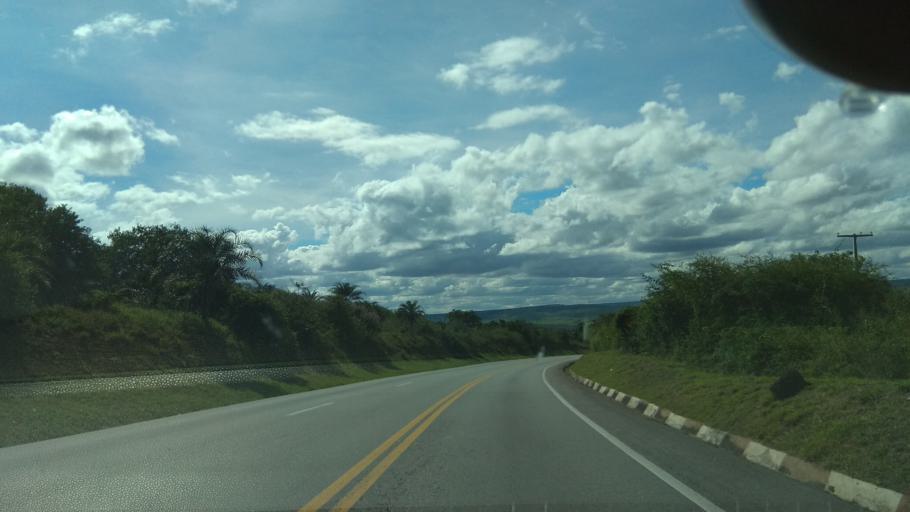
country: BR
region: Bahia
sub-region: Santa Ines
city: Santa Ines
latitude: -13.1847
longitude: -40.0060
